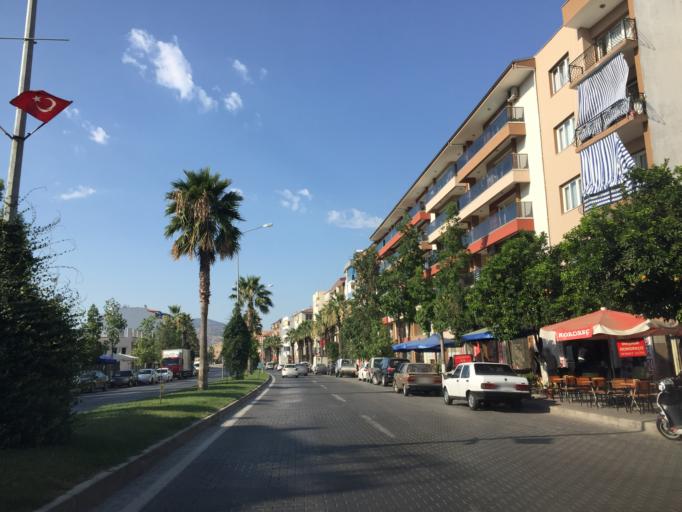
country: TR
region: Izmir
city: Selcuk
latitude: 37.9519
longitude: 27.3706
